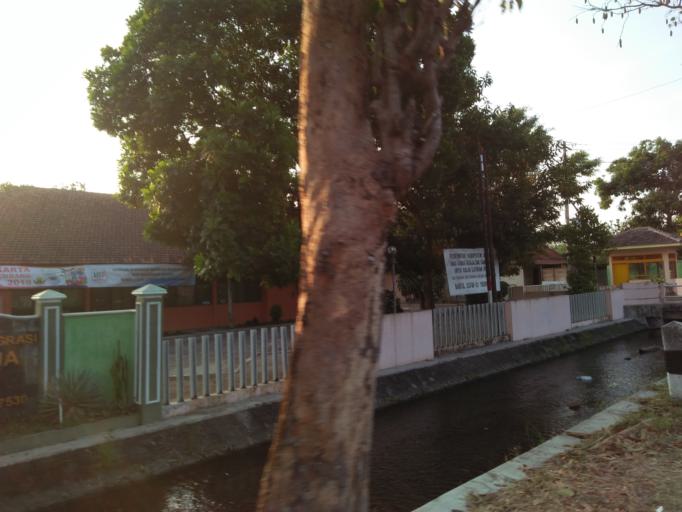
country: ID
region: Daerah Istimewa Yogyakarta
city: Bantul
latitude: -7.9064
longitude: 110.3523
